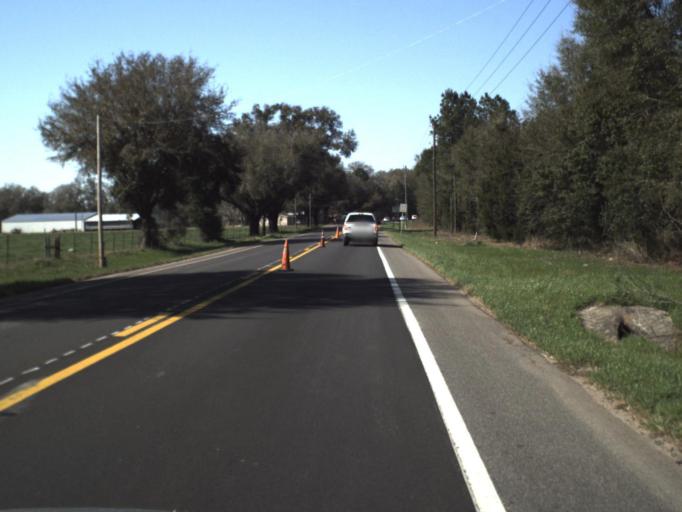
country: US
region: Florida
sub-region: Jackson County
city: Marianna
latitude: 30.6998
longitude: -85.1836
